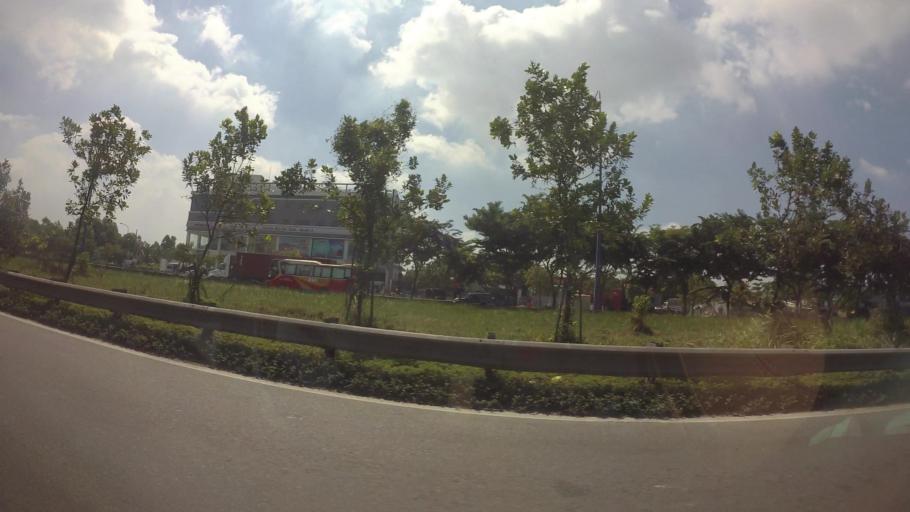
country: VN
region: Ho Chi Minh City
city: Quan Hai
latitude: 10.7987
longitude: 106.7527
